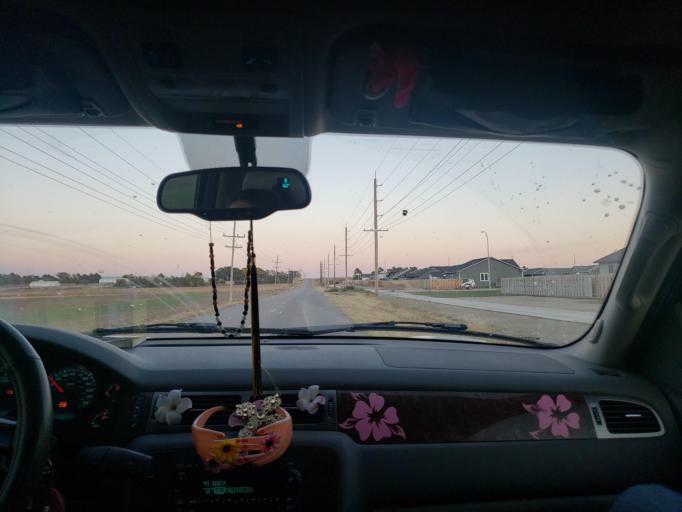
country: US
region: Kansas
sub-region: Finney County
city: Garden City
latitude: 37.9893
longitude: -100.8228
